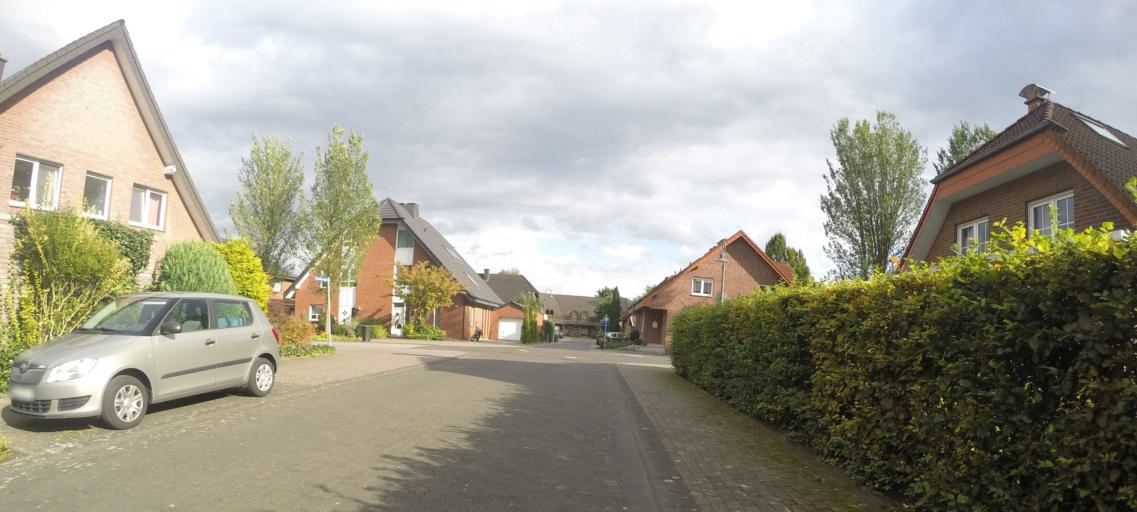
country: DE
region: North Rhine-Westphalia
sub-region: Regierungsbezirk Arnsberg
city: Lippstadt
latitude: 51.6877
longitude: 8.3582
